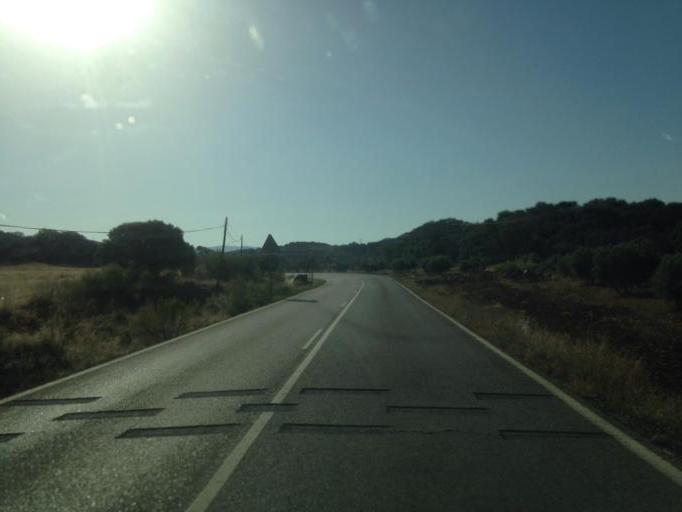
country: ES
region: Andalusia
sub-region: Provincia de Malaga
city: Archidona
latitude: 37.1060
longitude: -4.3553
